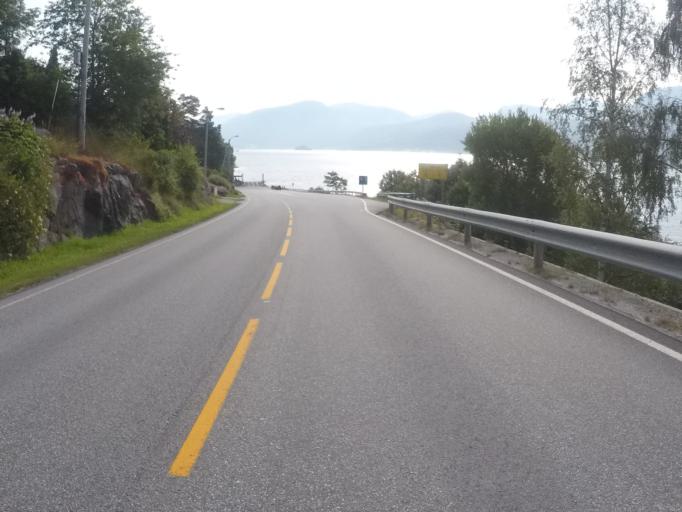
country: NO
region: More og Romsdal
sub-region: Molde
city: Hjelset
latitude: 62.6848
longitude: 7.4587
